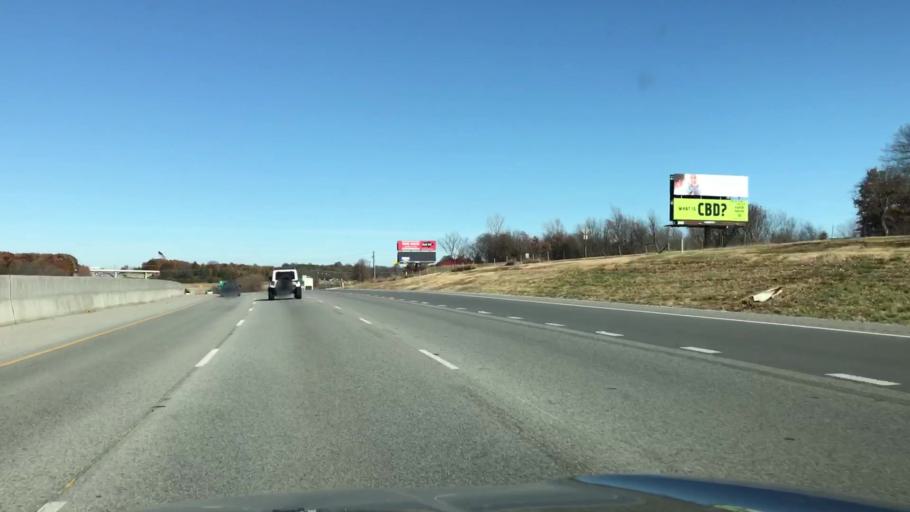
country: US
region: Arkansas
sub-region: Benton County
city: Lowell
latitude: 36.2466
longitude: -94.1507
